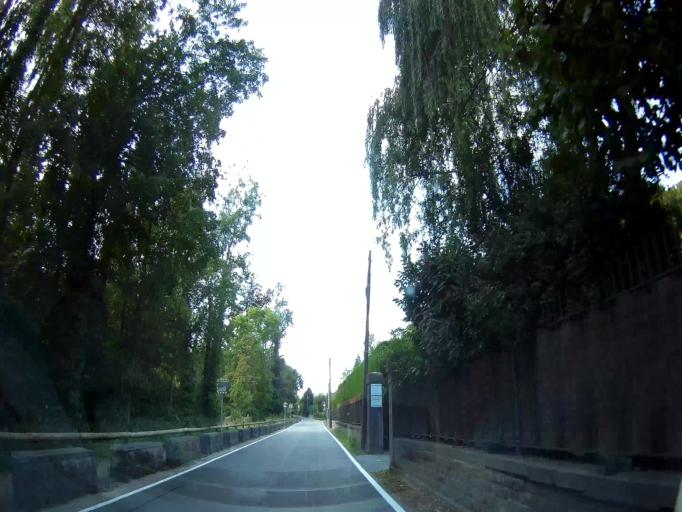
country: BE
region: Wallonia
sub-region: Province de Namur
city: Anhee
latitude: 50.3160
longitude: 4.8741
